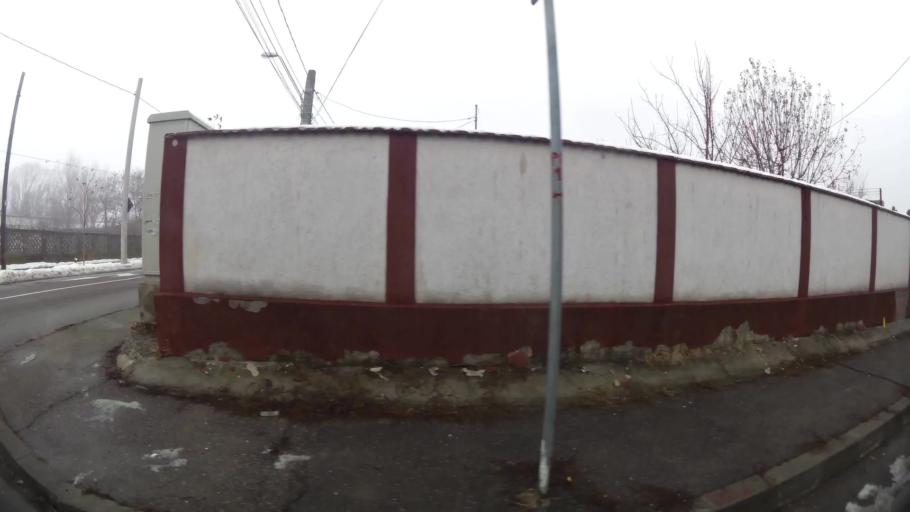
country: RO
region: Ilfov
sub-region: Comuna Chiajna
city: Rosu
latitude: 44.4674
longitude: 26.0105
